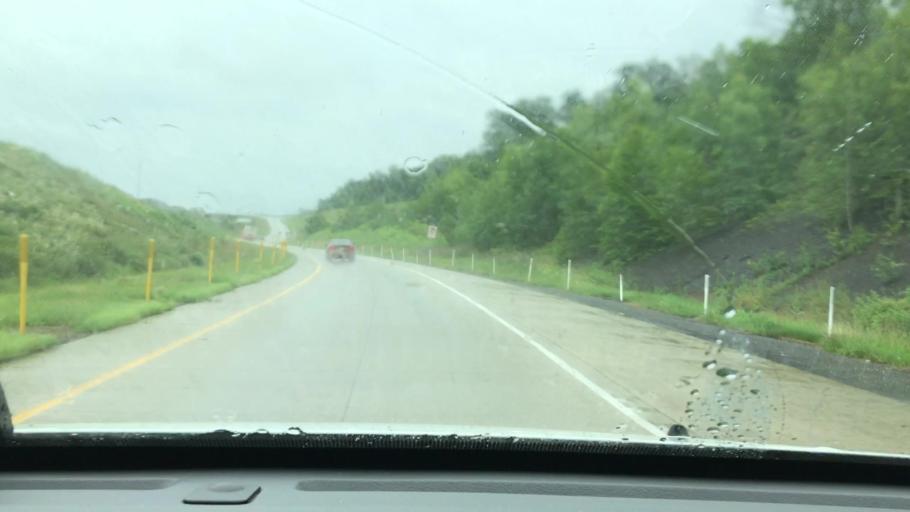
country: US
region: Pennsylvania
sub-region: Blair County
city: Tyrone
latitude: 40.7090
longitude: -78.1916
